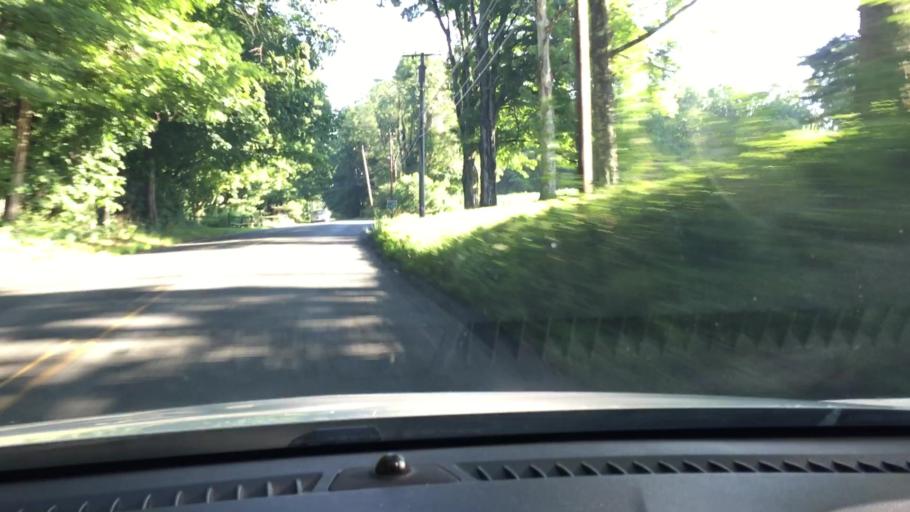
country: US
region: Massachusetts
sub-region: Berkshire County
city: Pittsfield
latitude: 42.4259
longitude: -73.2257
